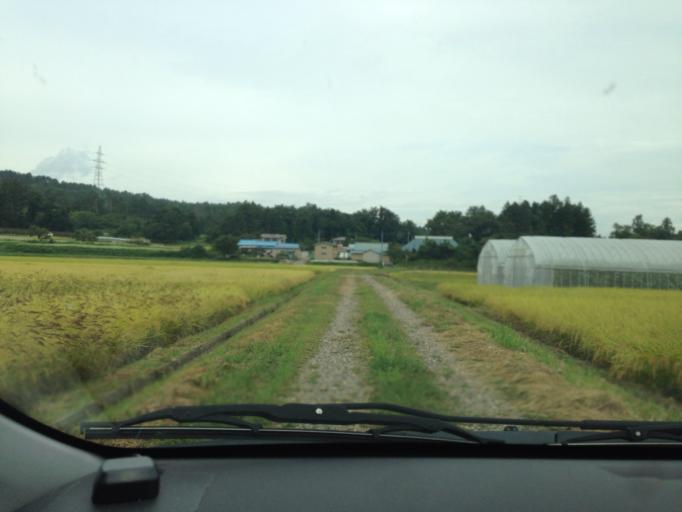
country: JP
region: Fukushima
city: Kitakata
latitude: 37.5872
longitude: 139.8080
